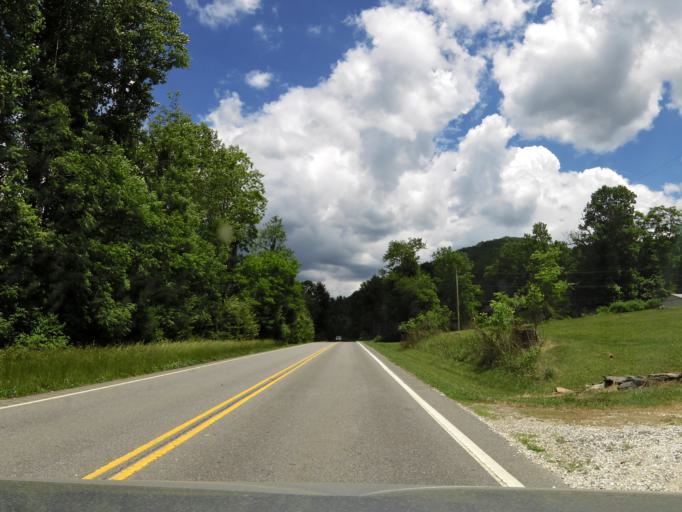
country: US
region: North Carolina
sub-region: Graham County
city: Robbinsville
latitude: 35.2682
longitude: -83.7154
